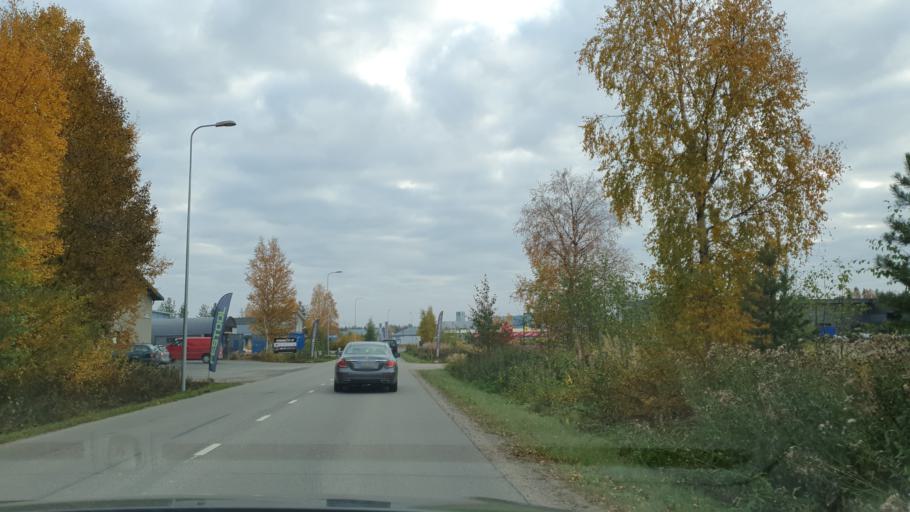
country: FI
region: Lapland
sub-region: Rovaniemi
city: Rovaniemi
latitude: 66.4931
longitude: 25.6790
